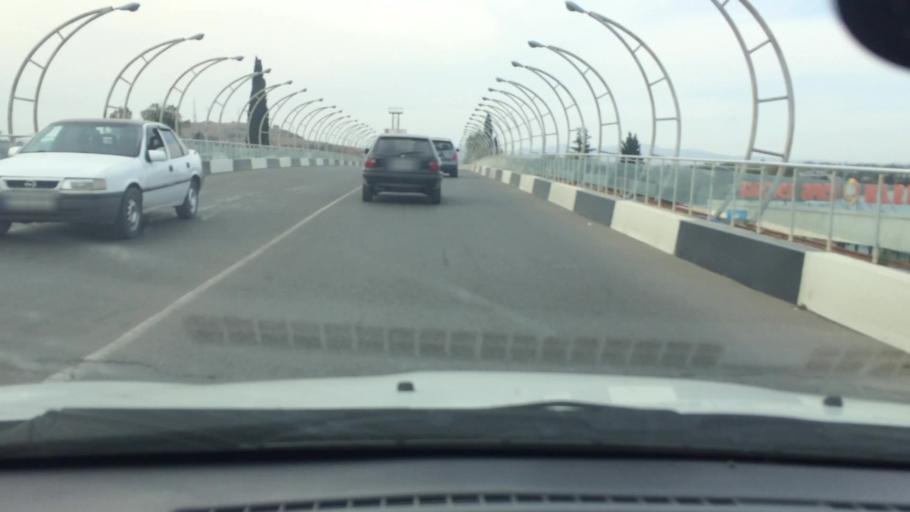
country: GE
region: Kvemo Kartli
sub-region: Marneuli
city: Marneuli
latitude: 41.4817
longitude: 44.8043
